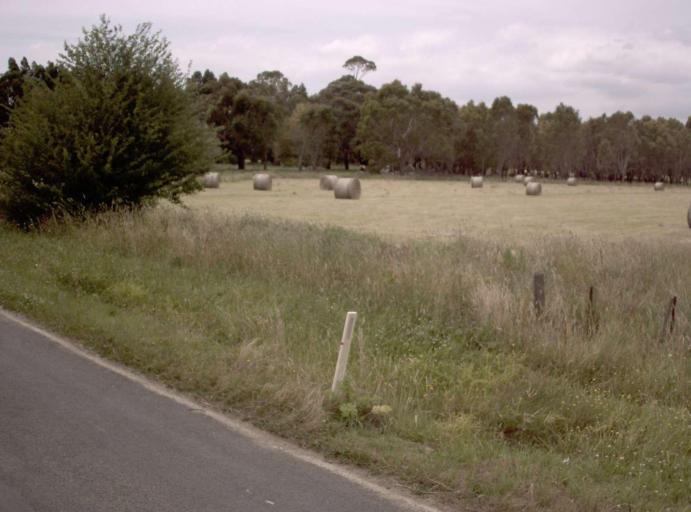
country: AU
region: Victoria
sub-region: Latrobe
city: Traralgon
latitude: -38.5122
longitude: 146.6625
